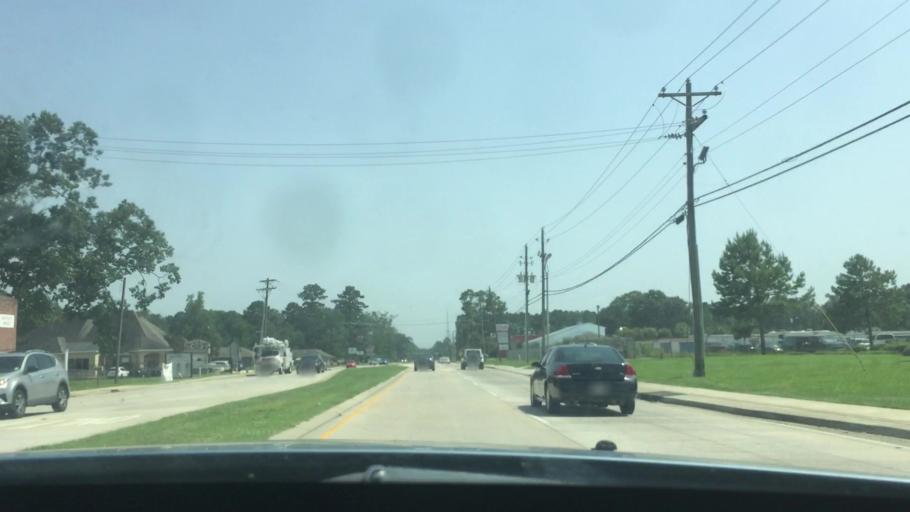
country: US
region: Louisiana
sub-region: East Baton Rouge Parish
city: Shenandoah
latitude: 30.4319
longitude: -91.0076
